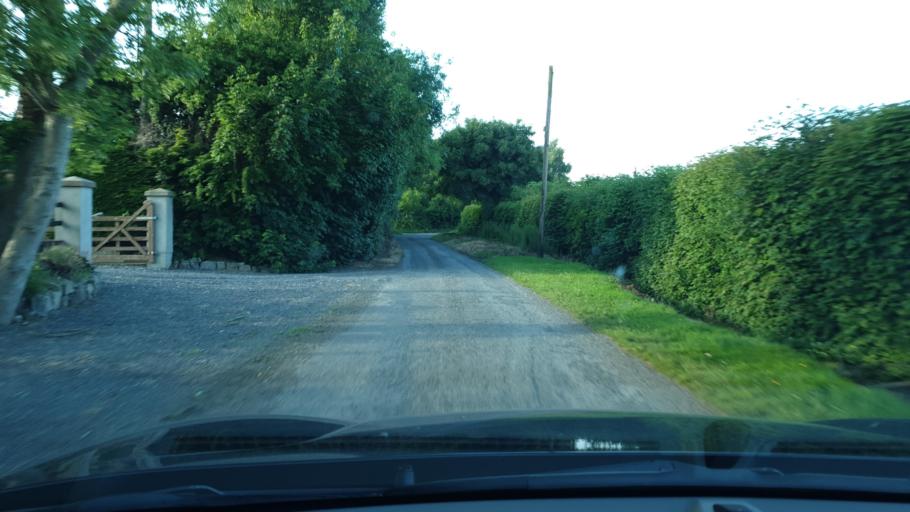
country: IE
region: Leinster
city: Hartstown
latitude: 53.4368
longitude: -6.4027
